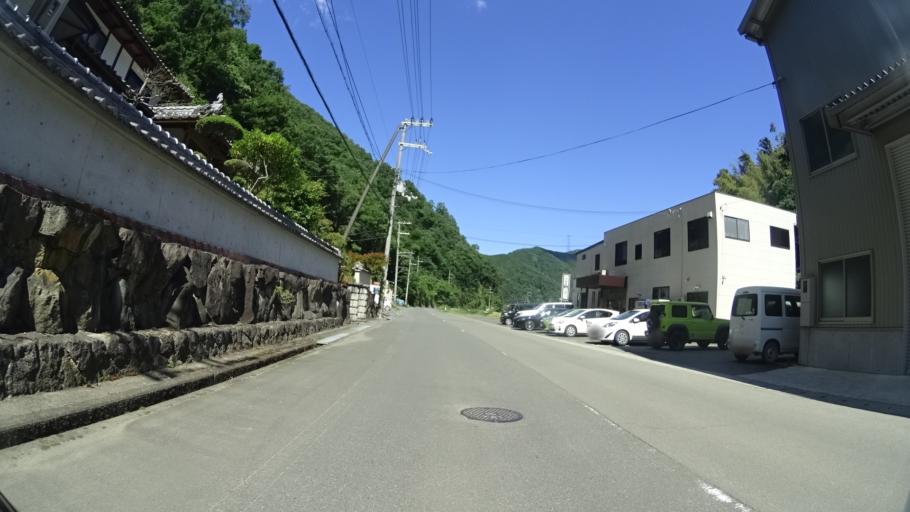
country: JP
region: Kyoto
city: Fukuchiyama
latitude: 35.3602
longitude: 135.1063
